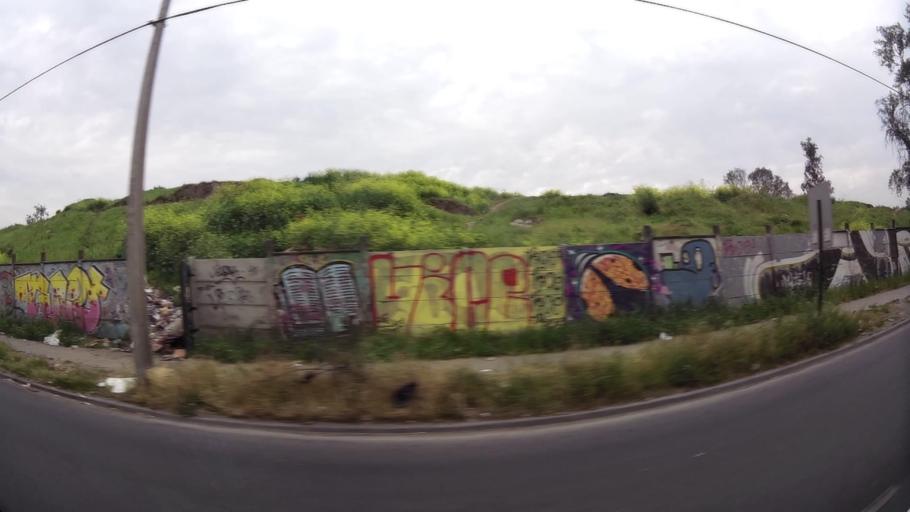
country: CL
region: Santiago Metropolitan
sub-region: Provincia de Santiago
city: Santiago
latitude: -33.4784
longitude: -70.6770
